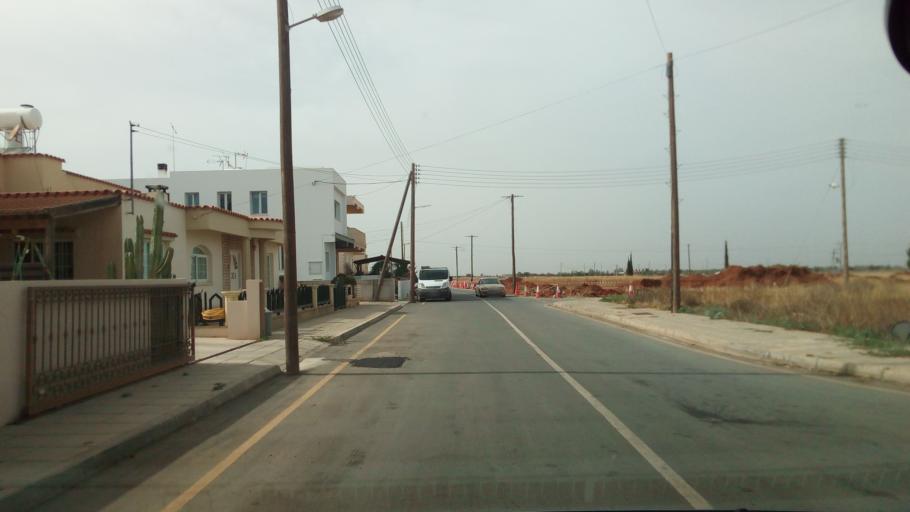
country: CY
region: Larnaka
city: Xylotymbou
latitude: 35.0222
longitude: 33.7430
